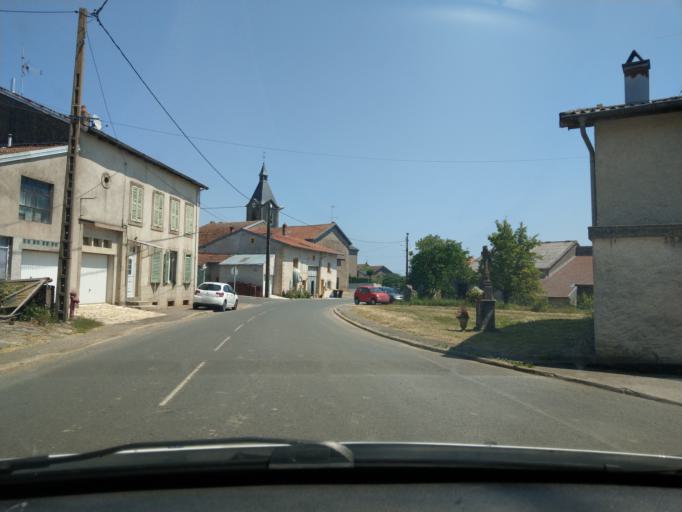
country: FR
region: Lorraine
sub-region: Departement de la Moselle
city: Lorquin
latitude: 48.6369
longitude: 6.8552
